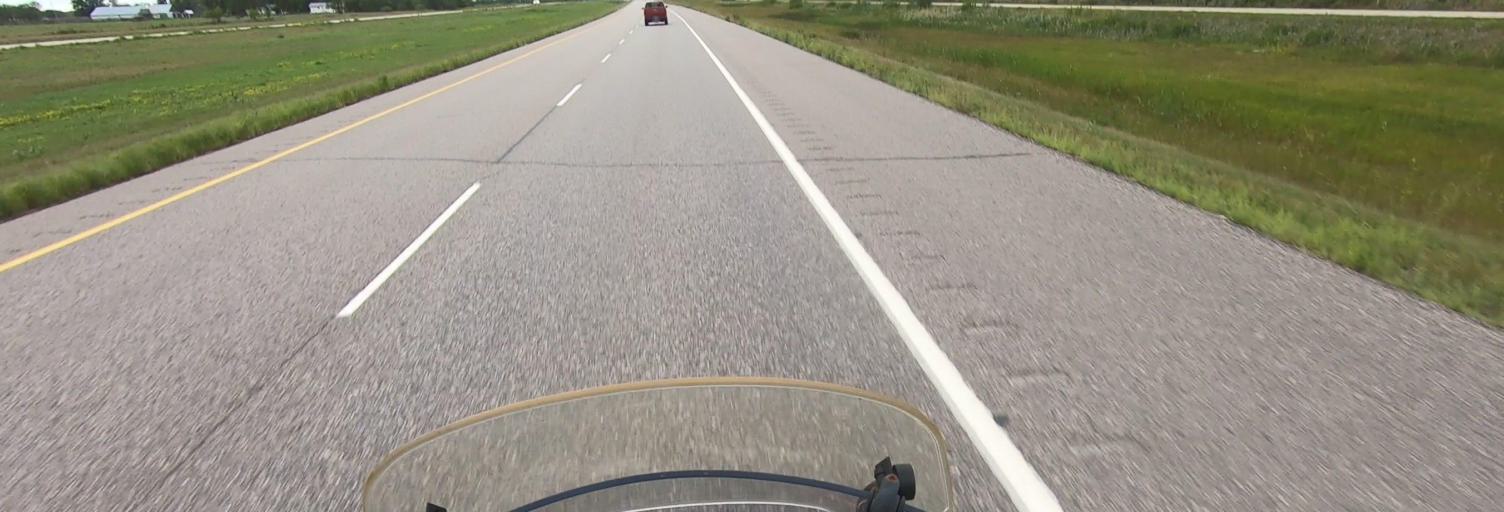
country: CA
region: Manitoba
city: Portage la Prairie
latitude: 49.9755
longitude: -98.6660
